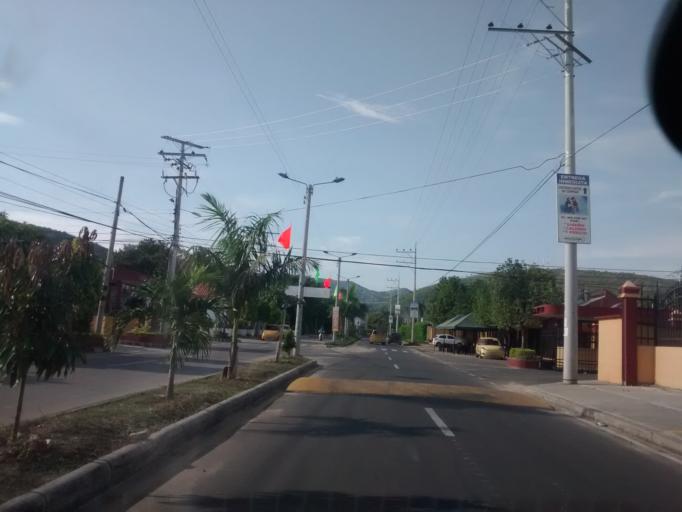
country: CO
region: Cundinamarca
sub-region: Girardot
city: Girardot City
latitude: 4.3082
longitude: -74.8146
